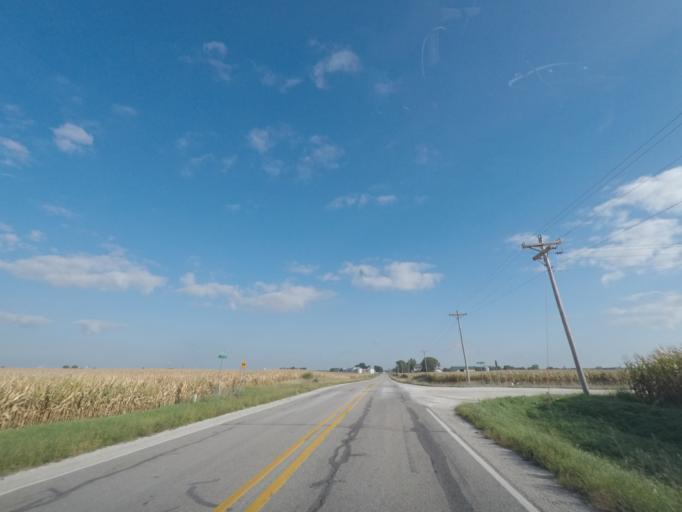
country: US
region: Iowa
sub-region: Story County
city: Nevada
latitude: 41.9935
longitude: -93.4629
